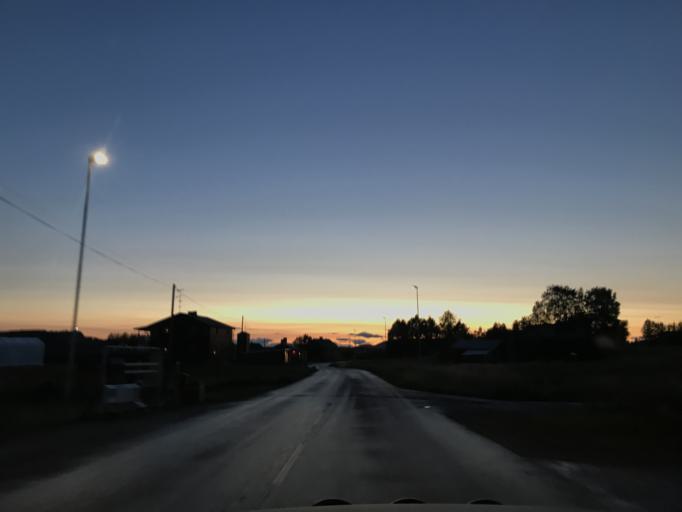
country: SE
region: Norrbotten
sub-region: Gallivare Kommun
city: Malmberget
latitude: 67.6452
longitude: 21.0542
